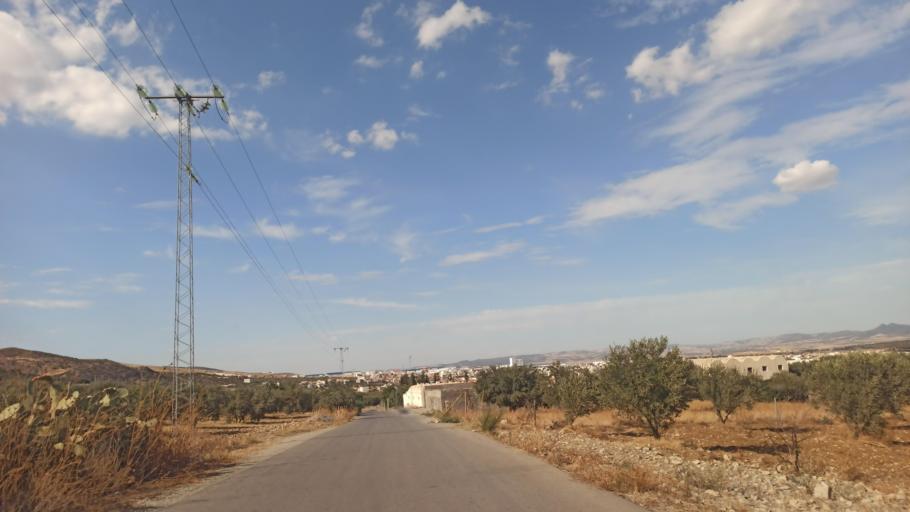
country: TN
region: Zaghwan
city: Zaghouan
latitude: 36.3368
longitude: 10.2107
